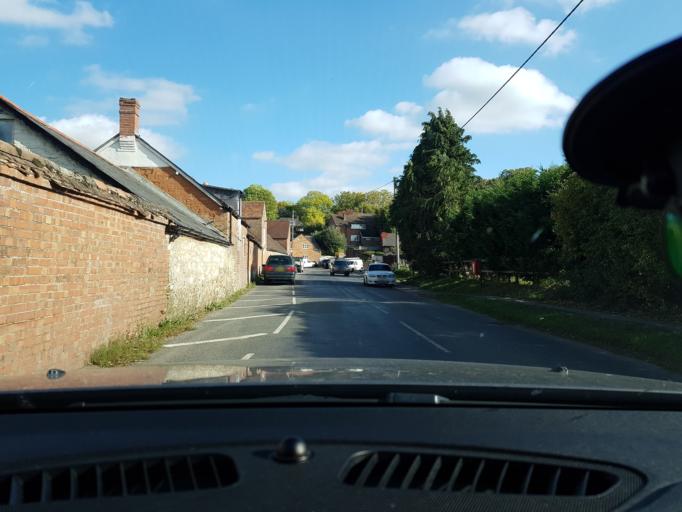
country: GB
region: England
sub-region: West Berkshire
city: Lambourn
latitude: 51.5067
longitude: -1.5343
